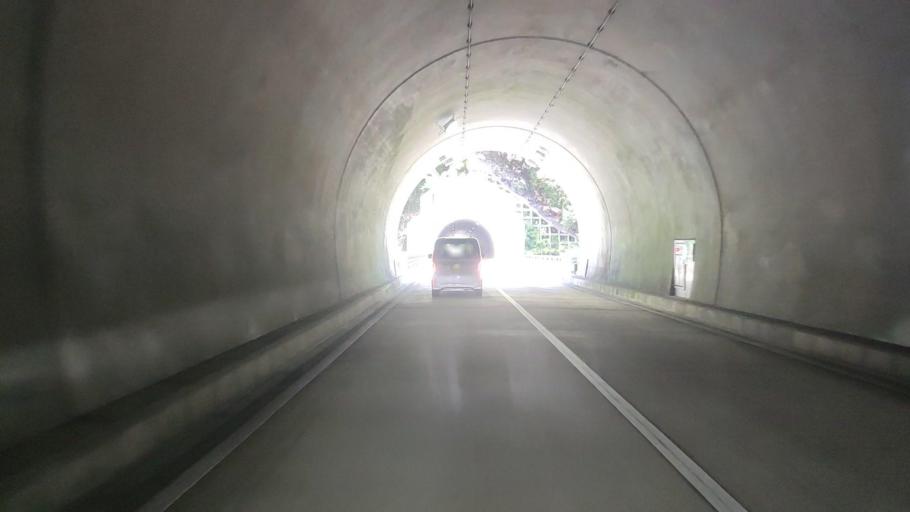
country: JP
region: Wakayama
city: Shingu
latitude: 33.8888
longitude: 135.8797
